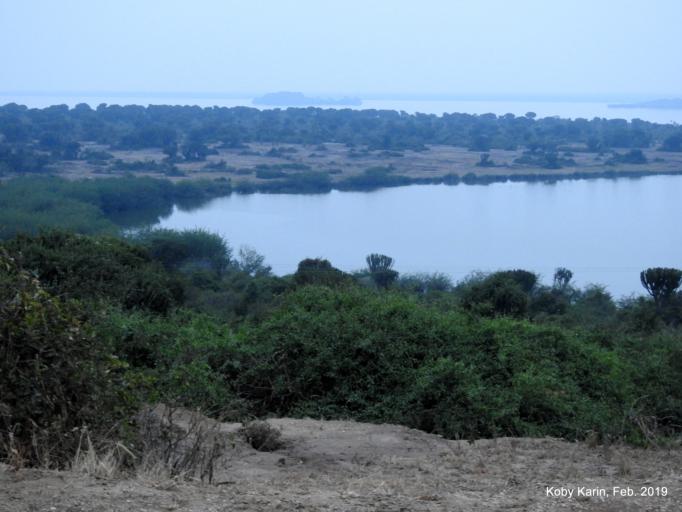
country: UG
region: Western Region
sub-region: Rubirizi District
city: Rubirizi
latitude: -0.1869
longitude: 29.8997
